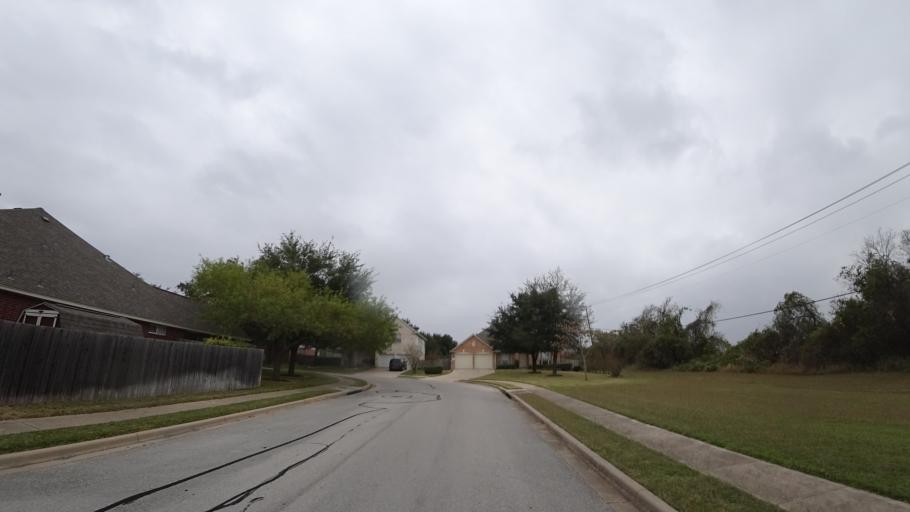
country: US
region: Texas
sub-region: Travis County
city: Pflugerville
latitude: 30.4326
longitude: -97.6175
